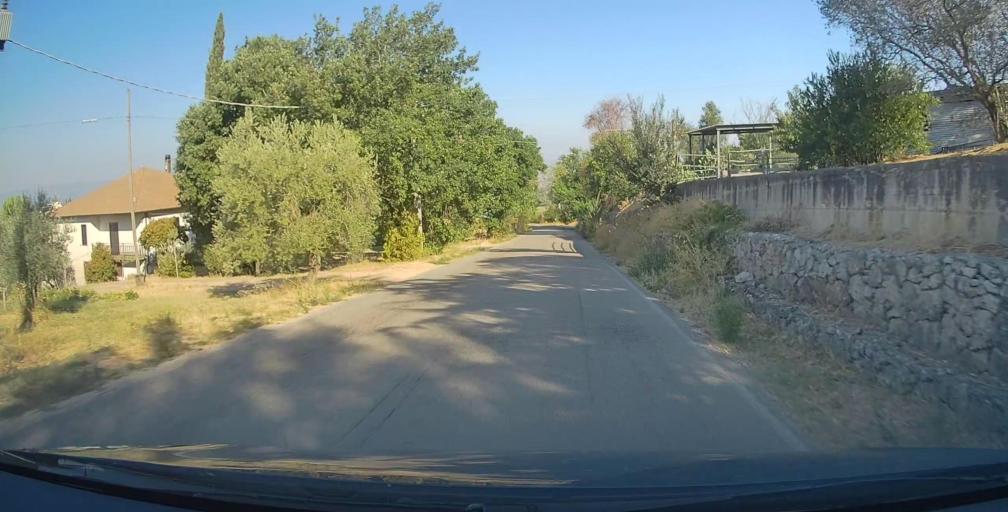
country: IT
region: Umbria
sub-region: Provincia di Terni
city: Calvi dell'Umbria
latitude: 42.4119
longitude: 12.5393
